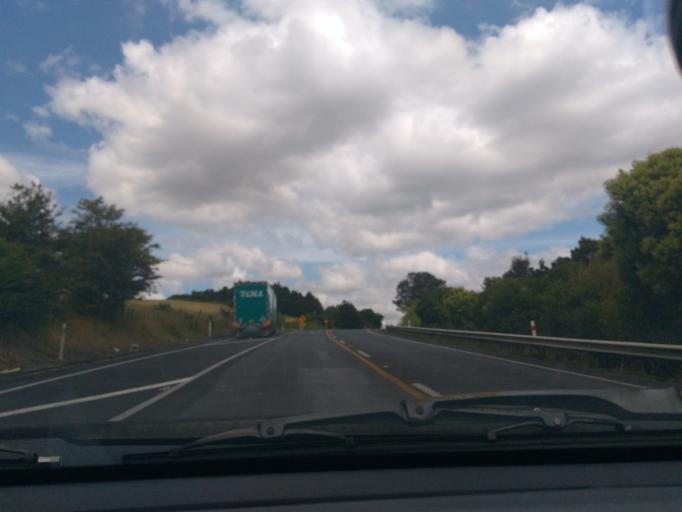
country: NZ
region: Northland
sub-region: Far North District
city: Moerewa
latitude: -35.3872
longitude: 173.9931
